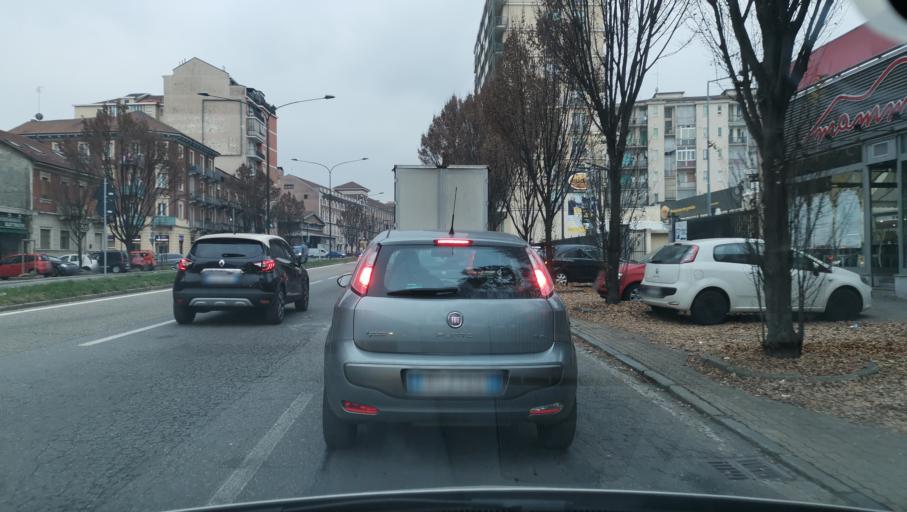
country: IT
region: Piedmont
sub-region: Provincia di Torino
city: Turin
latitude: 45.1074
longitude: 7.6969
